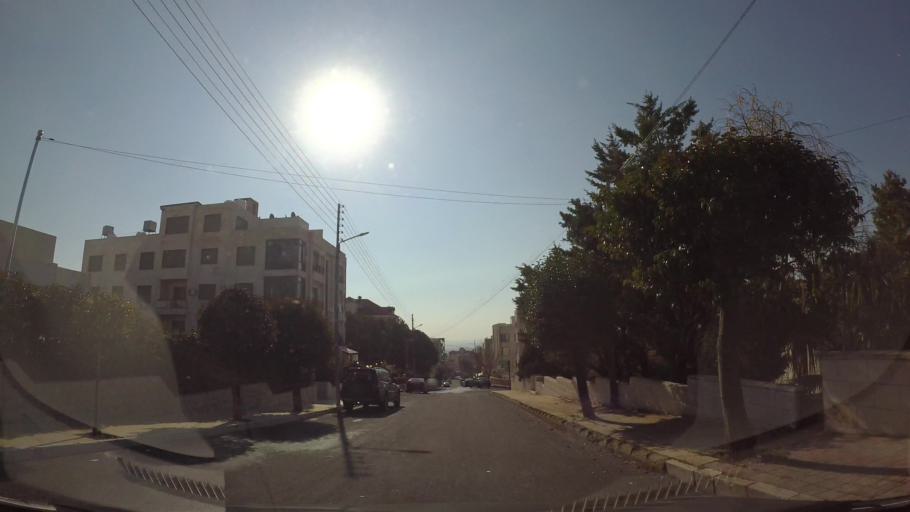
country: JO
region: Amman
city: Al Jubayhah
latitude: 31.9999
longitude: 35.8845
